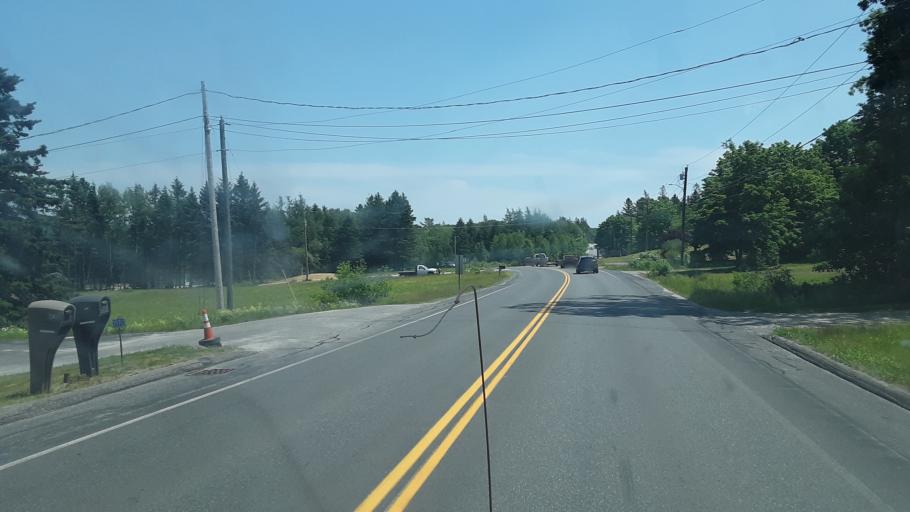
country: US
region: Maine
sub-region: Hancock County
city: Hancock
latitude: 44.5245
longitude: -68.2407
